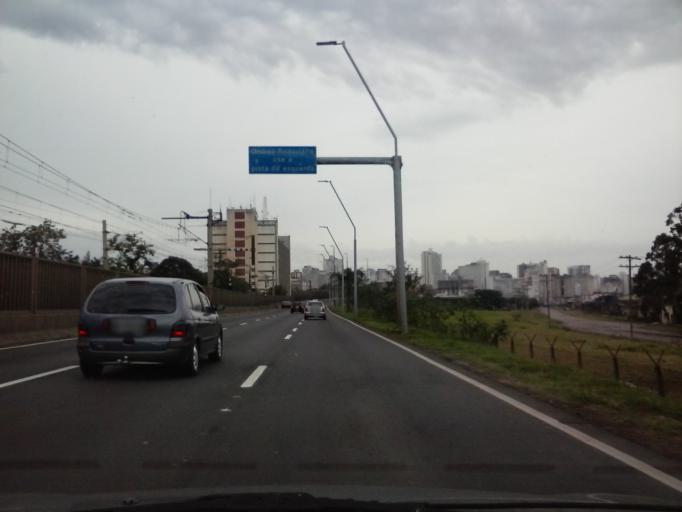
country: BR
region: Rio Grande do Sul
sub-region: Porto Alegre
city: Porto Alegre
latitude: -30.0182
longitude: -51.2158
